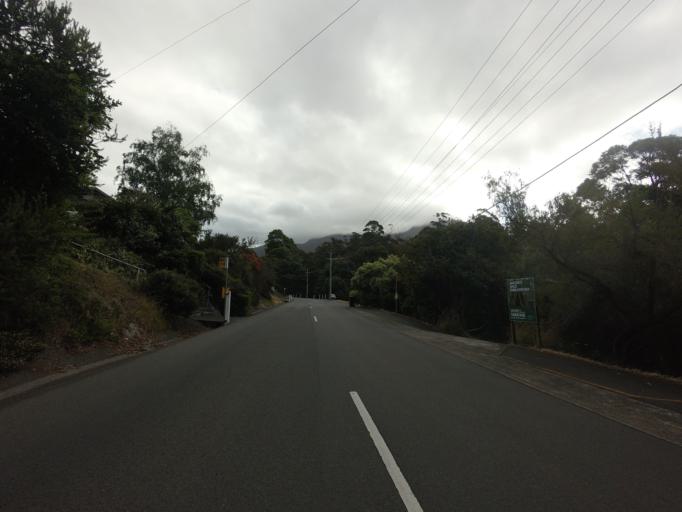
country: AU
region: Tasmania
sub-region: Hobart
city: Dynnyrne
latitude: -42.9018
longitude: 147.2801
